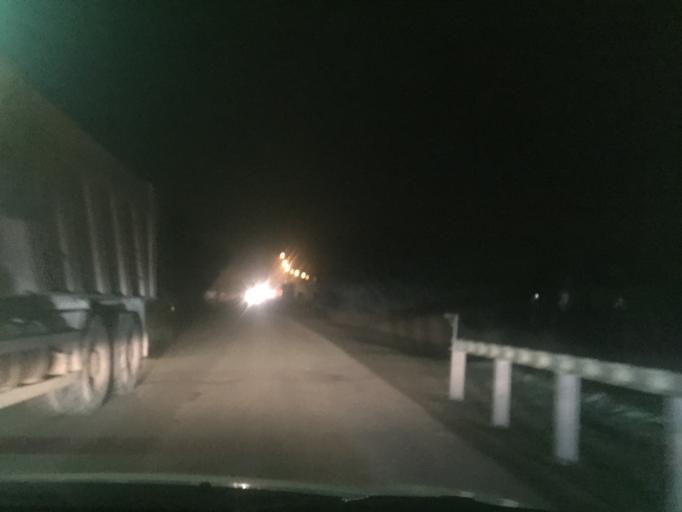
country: KZ
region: Astana Qalasy
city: Astana
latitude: 51.2073
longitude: 71.3801
